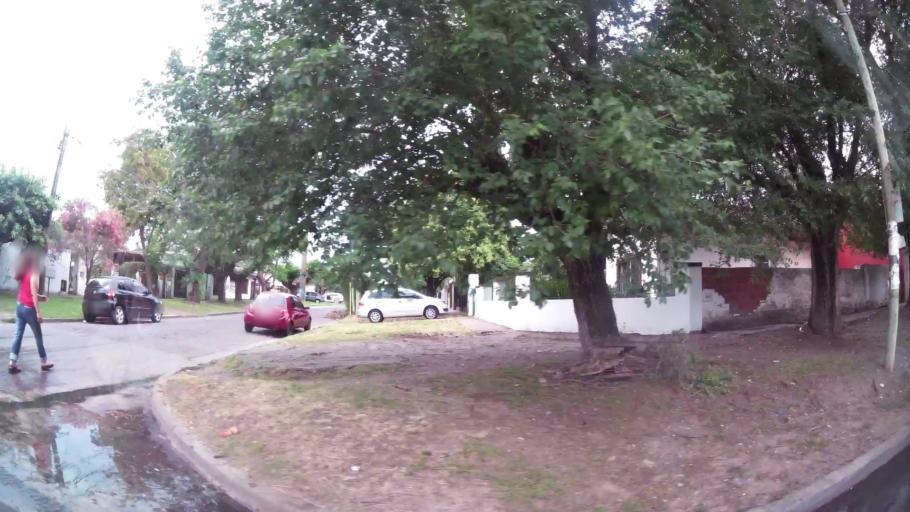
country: AR
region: Buenos Aires
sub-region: Partido de Tigre
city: Tigre
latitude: -34.4704
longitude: -58.6473
